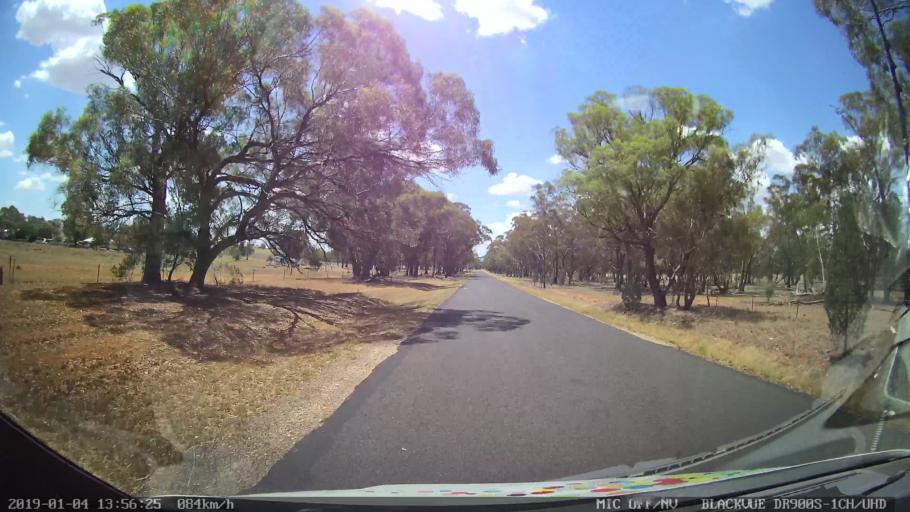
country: AU
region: New South Wales
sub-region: Dubbo Municipality
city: Dubbo
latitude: -32.3514
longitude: 148.5938
